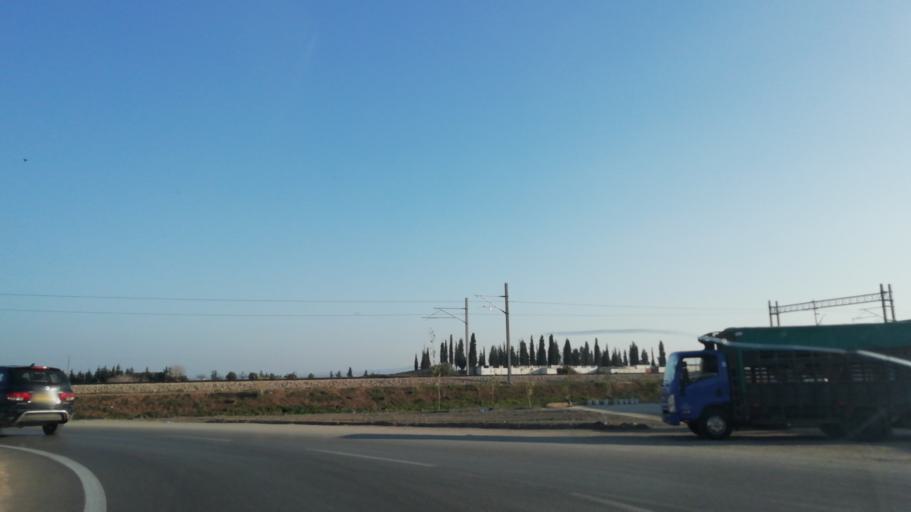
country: DZ
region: Sidi Bel Abbes
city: Sidi Bel Abbes
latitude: 35.1669
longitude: -0.6866
